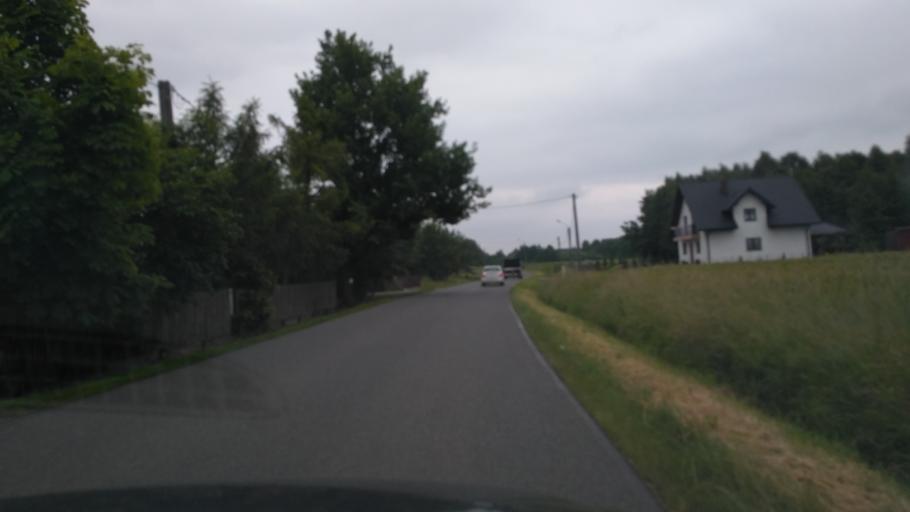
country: PL
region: Subcarpathian Voivodeship
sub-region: Powiat kolbuszowski
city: Niwiska
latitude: 50.1634
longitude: 21.6685
